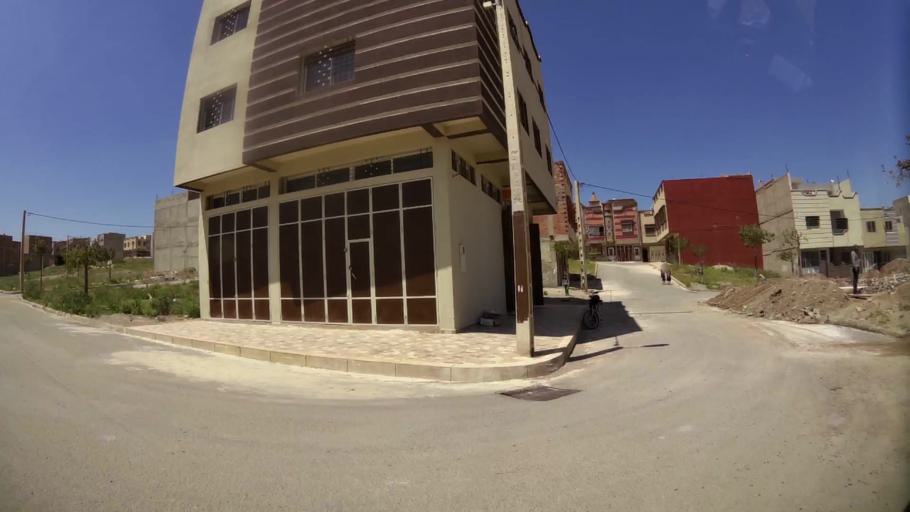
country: MA
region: Oriental
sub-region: Oujda-Angad
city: Oujda
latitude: 34.6781
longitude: -1.9507
